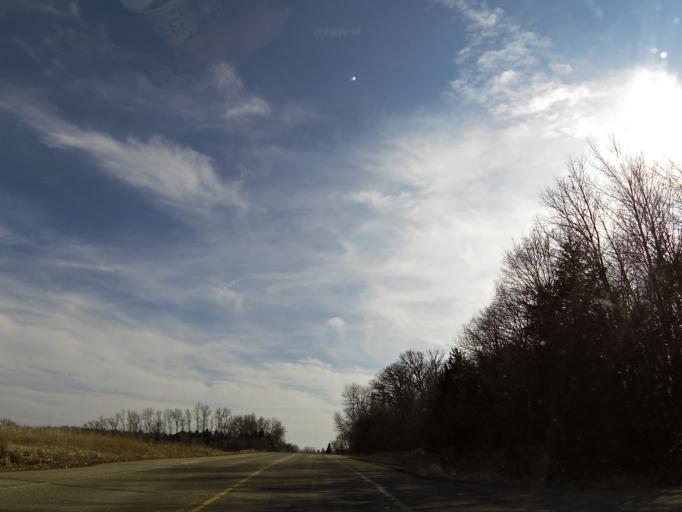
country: US
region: Minnesota
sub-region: Scott County
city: Prior Lake
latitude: 44.6445
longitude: -93.4704
